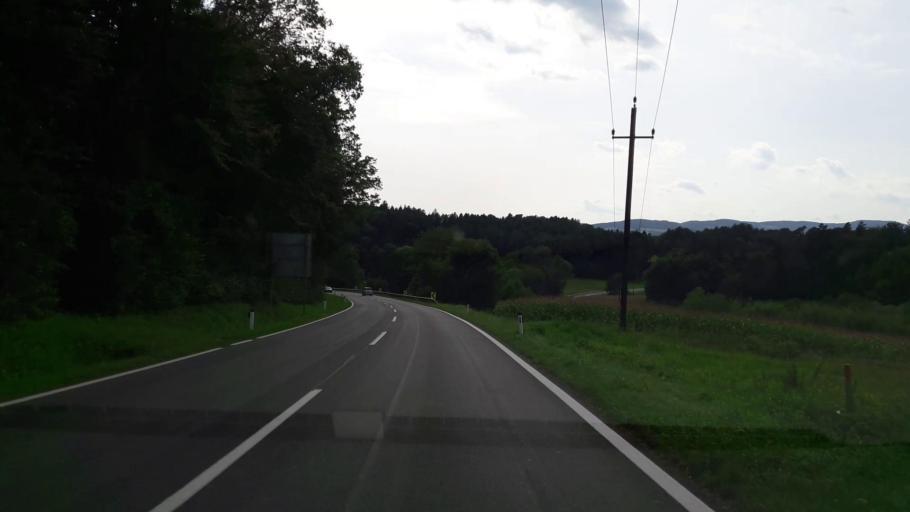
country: AT
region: Styria
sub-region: Politischer Bezirk Hartberg-Fuerstenfeld
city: Hartberg
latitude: 47.2664
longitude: 15.9416
